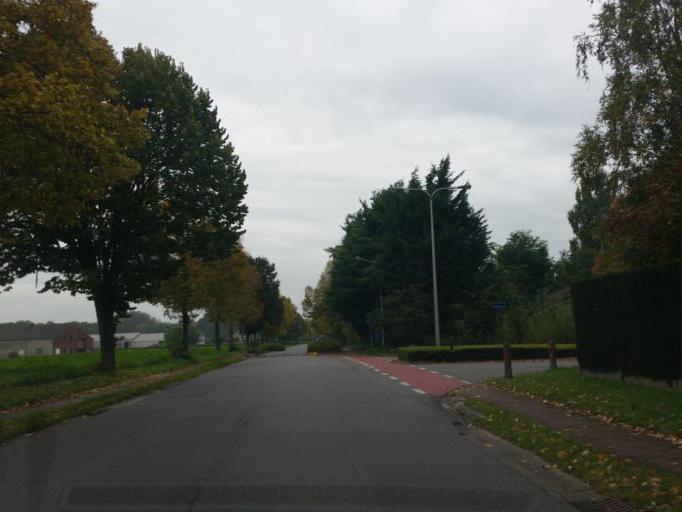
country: BE
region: Flanders
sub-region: Provincie Vlaams-Brabant
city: Steenokkerzeel
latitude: 50.9244
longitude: 4.4951
